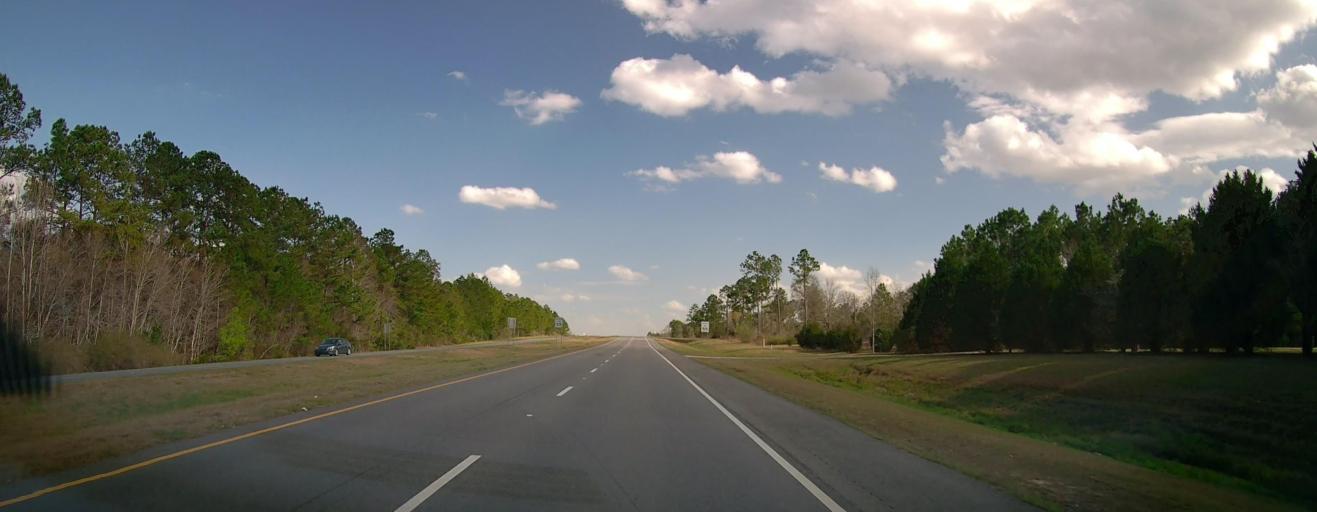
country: US
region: Georgia
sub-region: Telfair County
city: Helena
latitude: 32.0876
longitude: -82.9353
